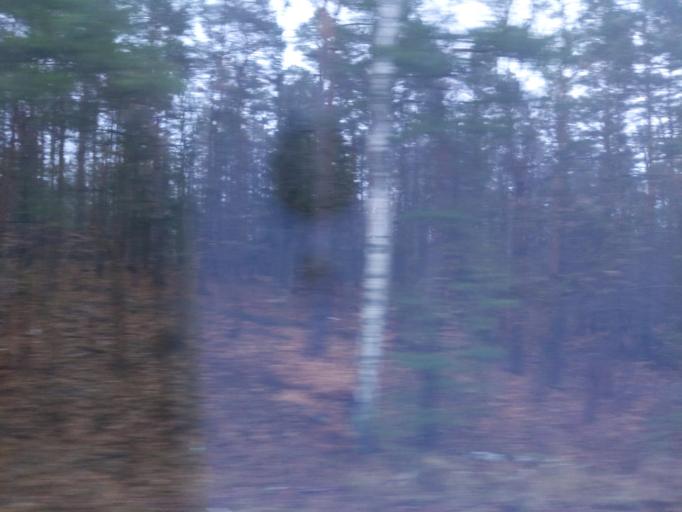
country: DE
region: Saxony
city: Albertstadt
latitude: 51.1081
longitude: 13.7883
